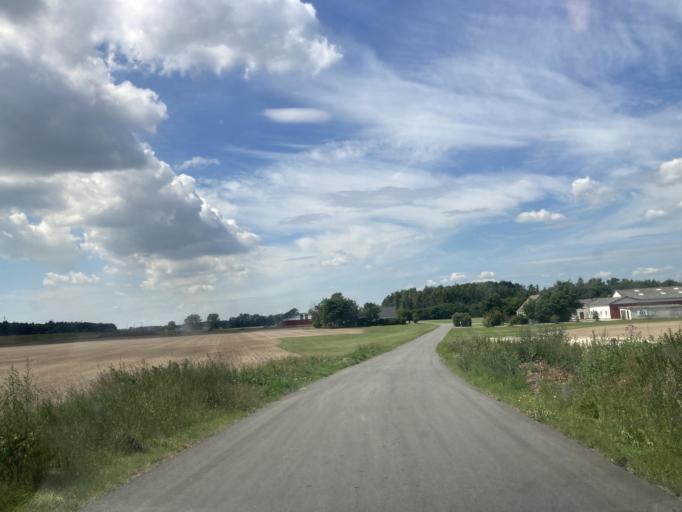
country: DK
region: Zealand
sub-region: Koge Kommune
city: Borup
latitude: 55.4597
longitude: 11.9812
